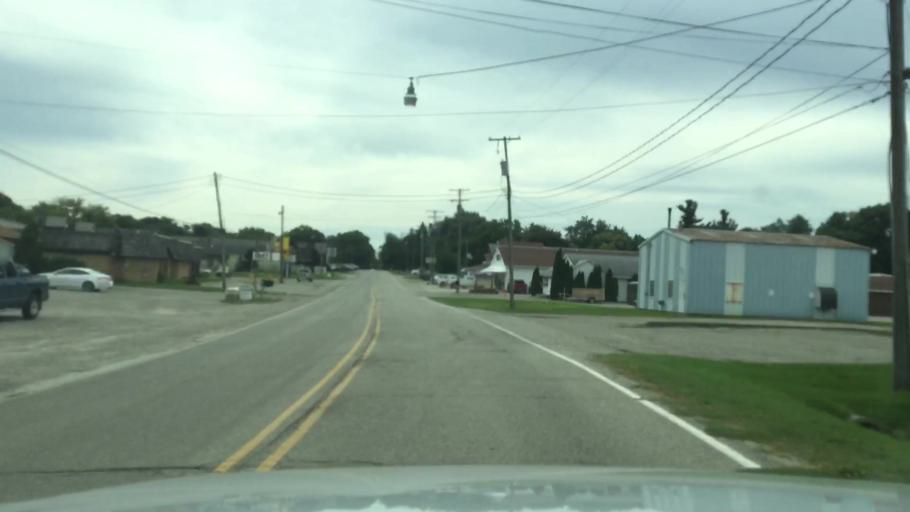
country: US
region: Michigan
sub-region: Shiawassee County
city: Durand
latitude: 42.9226
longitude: -83.9851
